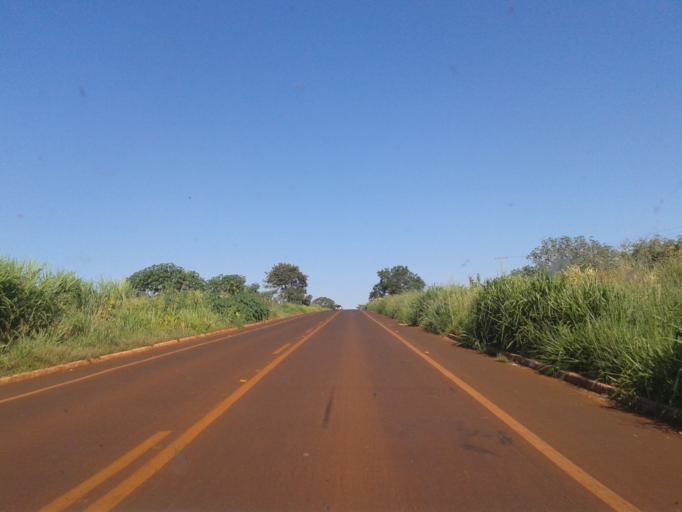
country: BR
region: Minas Gerais
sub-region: Capinopolis
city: Capinopolis
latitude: -18.7028
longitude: -49.6704
